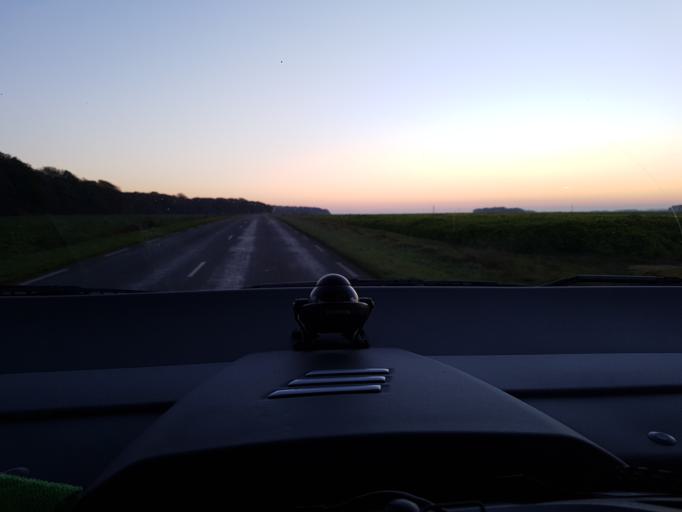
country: FR
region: Picardie
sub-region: Departement de la Somme
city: Rue
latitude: 50.2998
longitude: 1.7480
